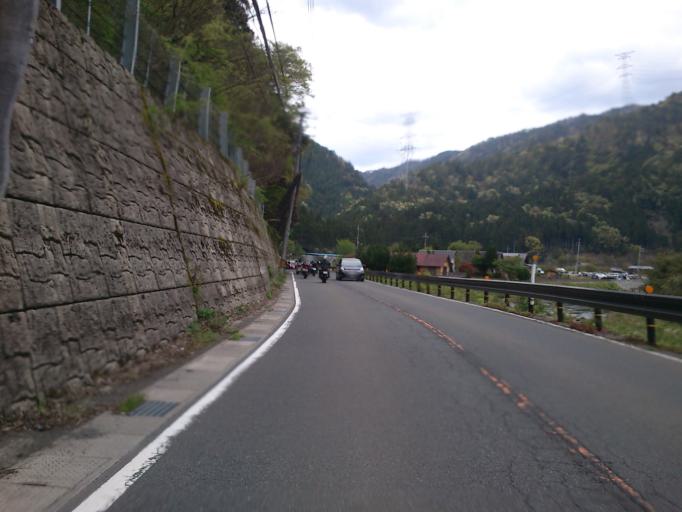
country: JP
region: Fukui
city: Obama
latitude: 35.3073
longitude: 135.6231
